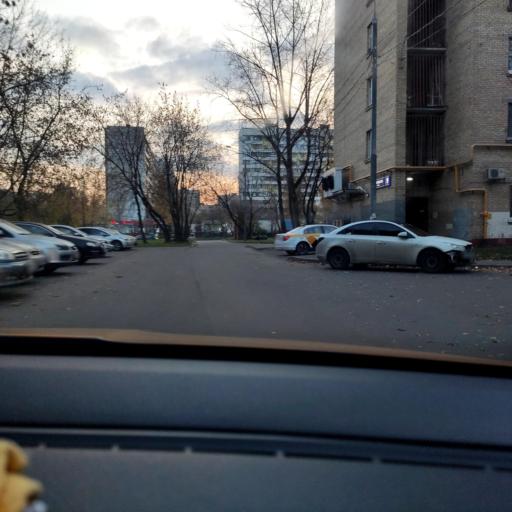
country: RU
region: Moscow
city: Gol'yanovo
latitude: 55.8196
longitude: 37.8245
